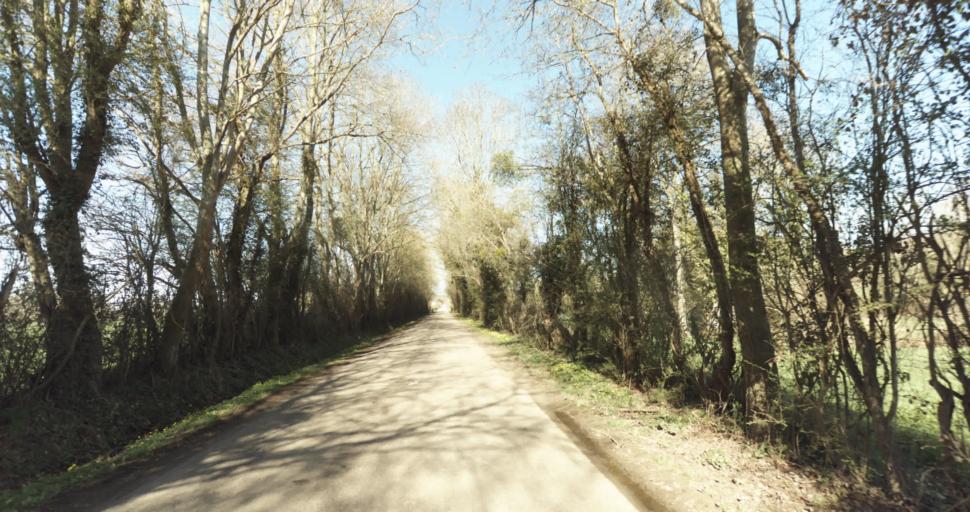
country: FR
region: Lower Normandy
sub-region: Departement du Calvados
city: Saint-Pierre-sur-Dives
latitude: 48.9705
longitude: 0.0484
